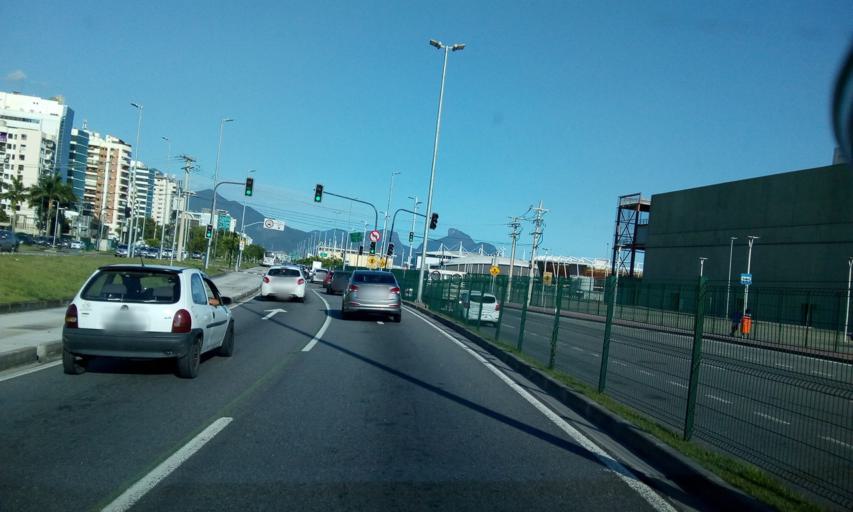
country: BR
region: Rio de Janeiro
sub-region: Nilopolis
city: Nilopolis
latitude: -22.9734
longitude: -43.3990
